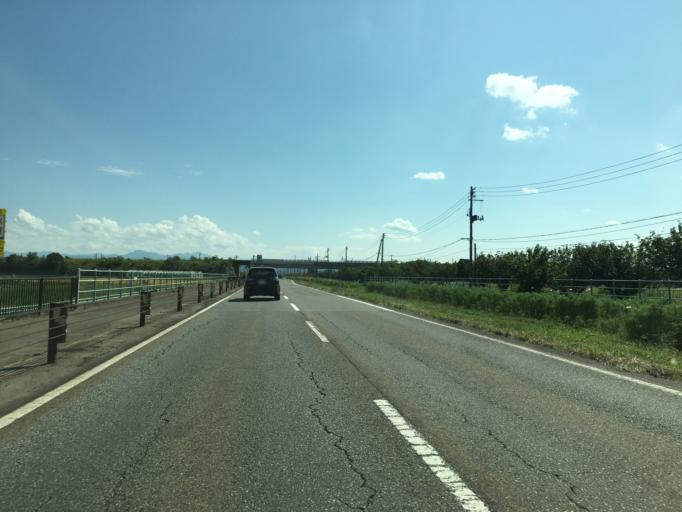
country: JP
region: Niigata
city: Niitsu-honcho
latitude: 37.8235
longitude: 139.0986
